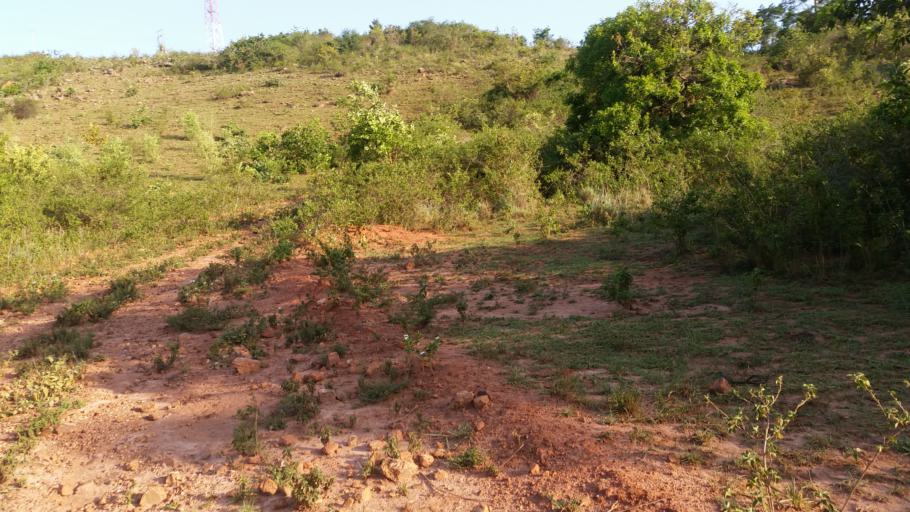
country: UG
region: Eastern Region
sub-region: Busia District
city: Busia
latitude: 0.5433
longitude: 34.0145
